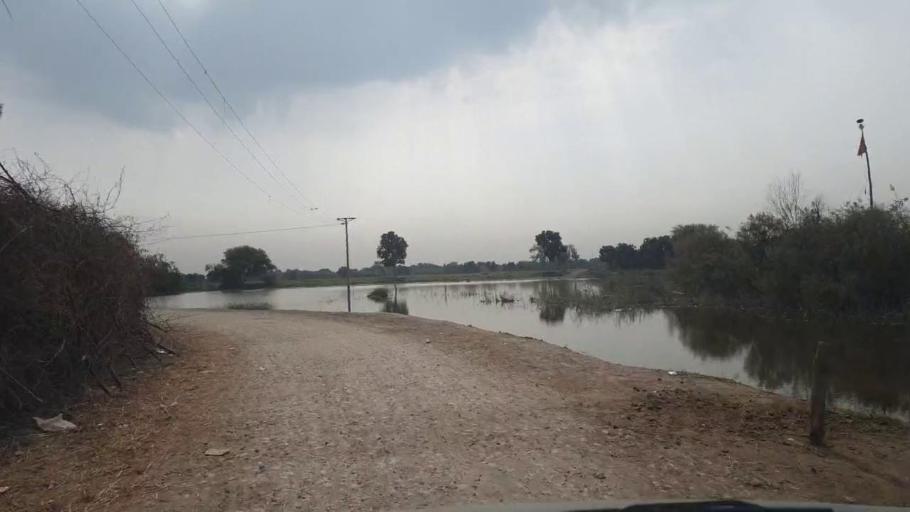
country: PK
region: Sindh
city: Matli
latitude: 24.9561
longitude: 68.7118
